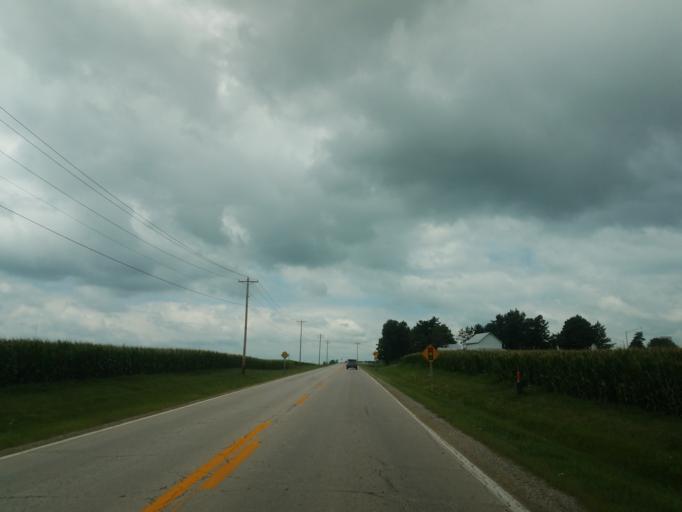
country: US
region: Illinois
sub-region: McLean County
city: Bloomington
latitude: 40.4846
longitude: -89.0343
